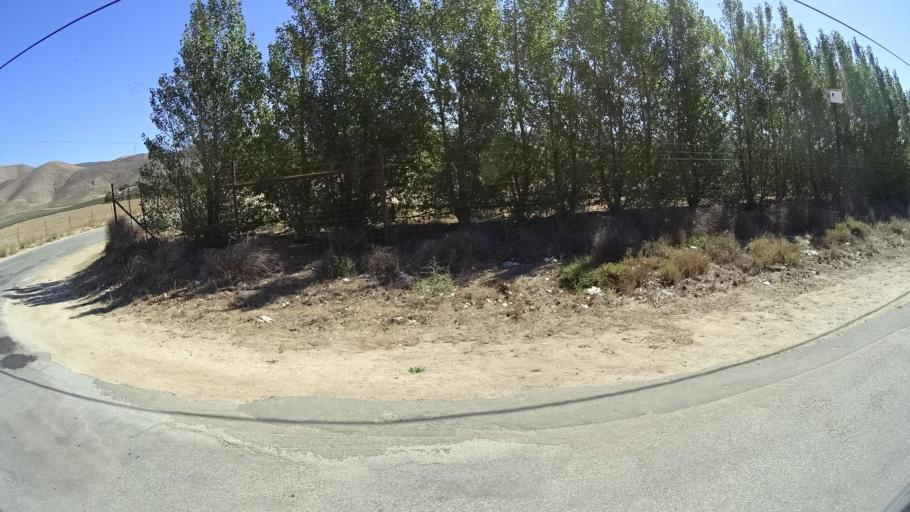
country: US
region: California
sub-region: Monterey County
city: Soledad
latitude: 36.4450
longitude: -121.3118
